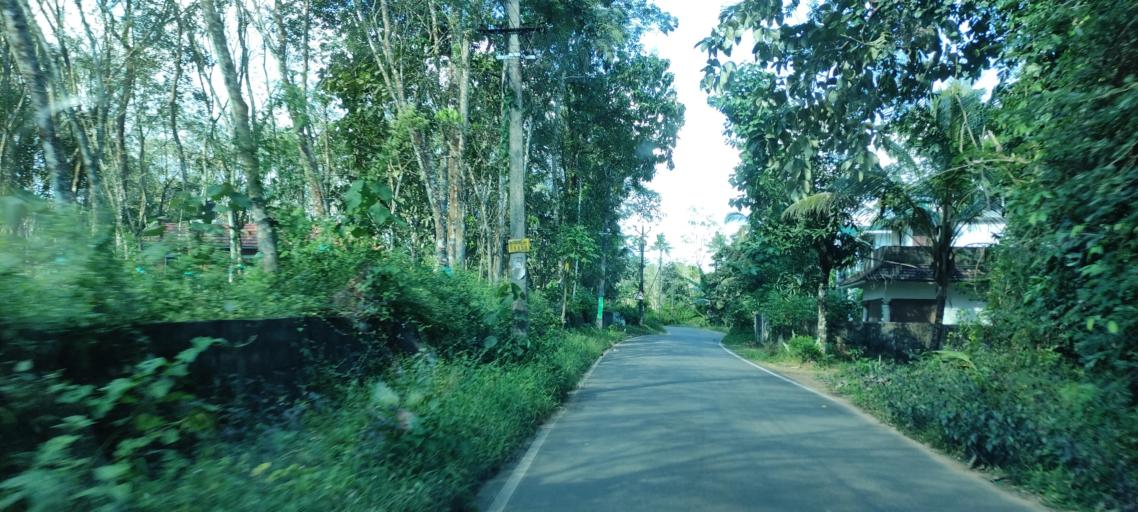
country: IN
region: Kerala
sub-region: Pattanamtitta
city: Adur
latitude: 9.2040
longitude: 76.7484
